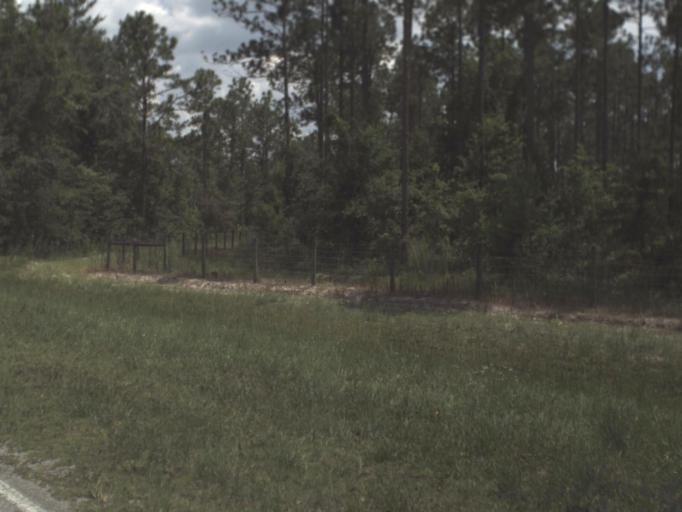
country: US
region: Florida
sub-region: Bradford County
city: Starke
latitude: 29.9831
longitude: -82.0153
